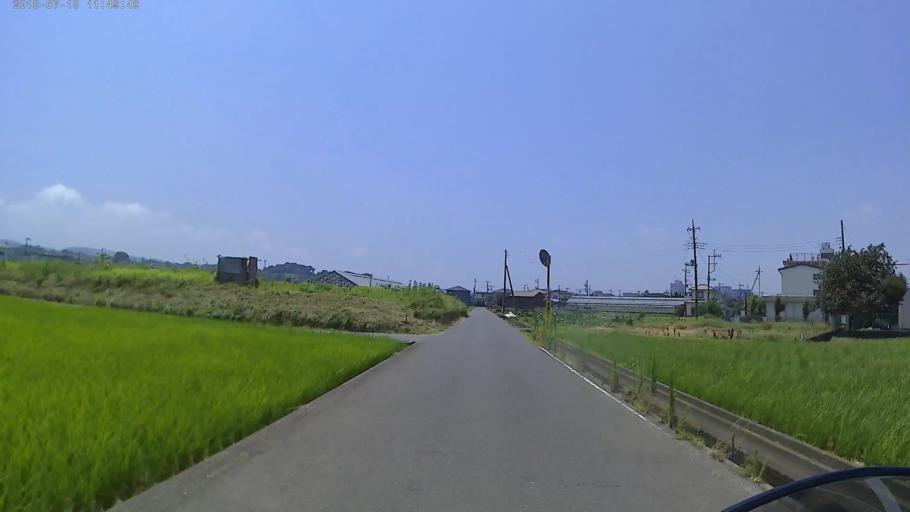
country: JP
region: Kanagawa
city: Isehara
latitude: 35.3634
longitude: 139.2894
